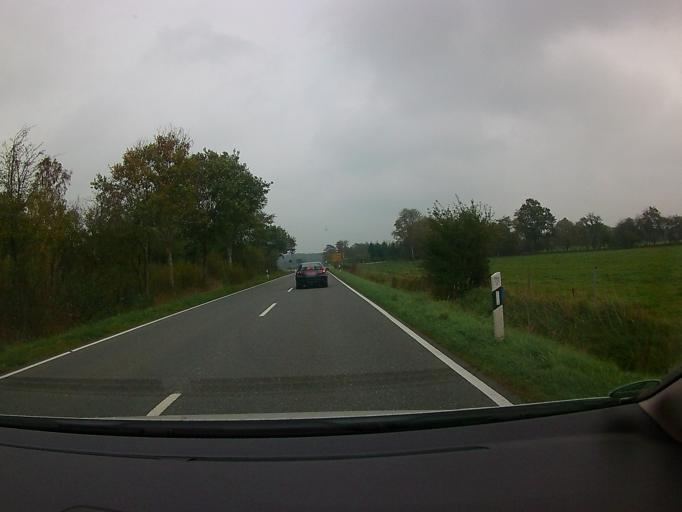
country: DE
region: Schleswig-Holstein
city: Lindewitt
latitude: 54.6883
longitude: 9.2006
